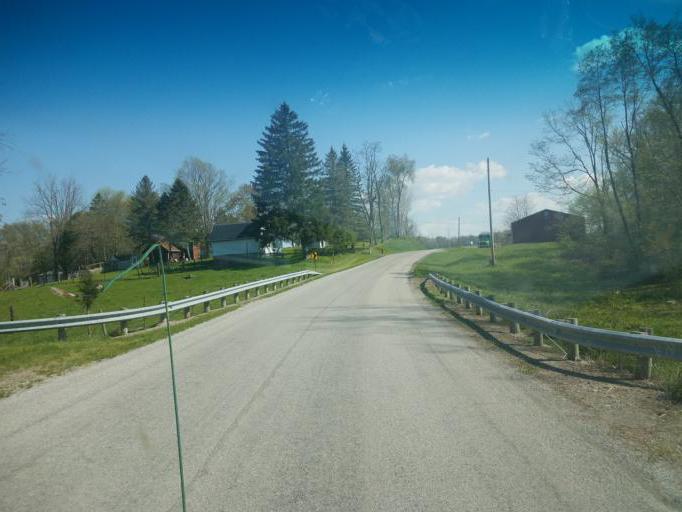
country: US
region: Ohio
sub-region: Medina County
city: Westfield Center
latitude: 40.9887
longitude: -81.9391
